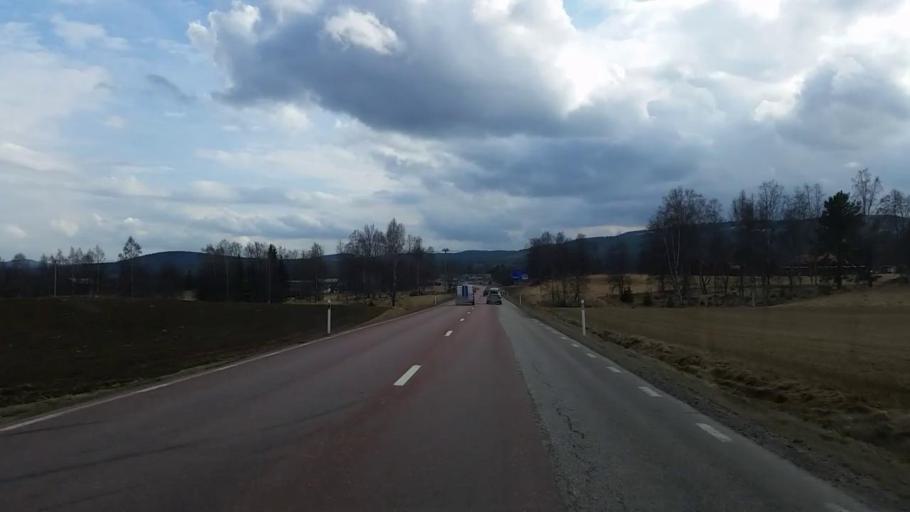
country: SE
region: Gaevleborg
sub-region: Ljusdals Kommun
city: Jaervsoe
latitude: 61.6786
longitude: 16.1453
